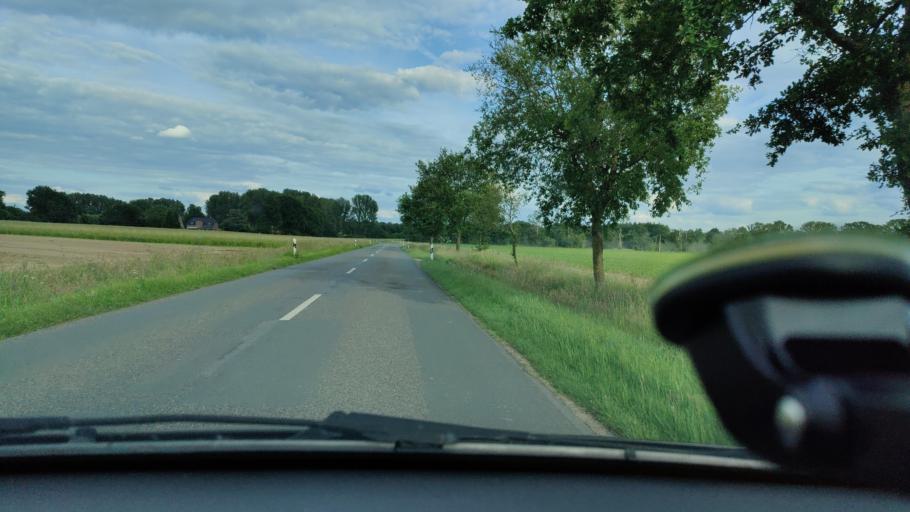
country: DE
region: North Rhine-Westphalia
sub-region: Regierungsbezirk Dusseldorf
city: Weeze
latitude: 51.6271
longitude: 6.1612
